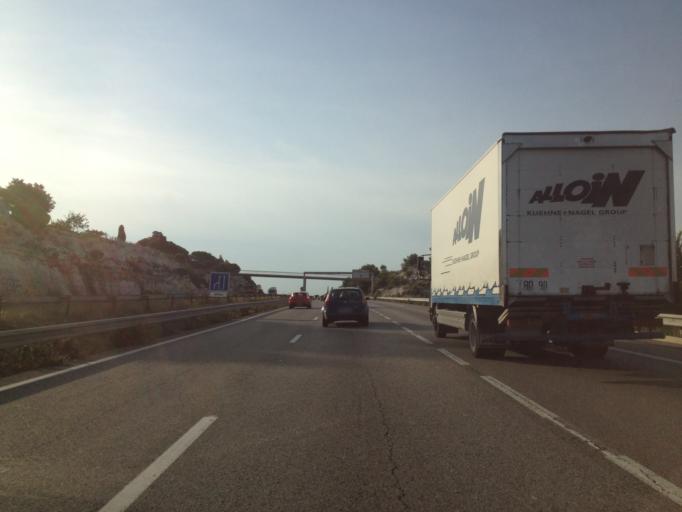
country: FR
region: Provence-Alpes-Cote d'Azur
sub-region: Departement des Bouches-du-Rhone
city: Vitrolles
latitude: 43.4519
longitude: 5.2380
